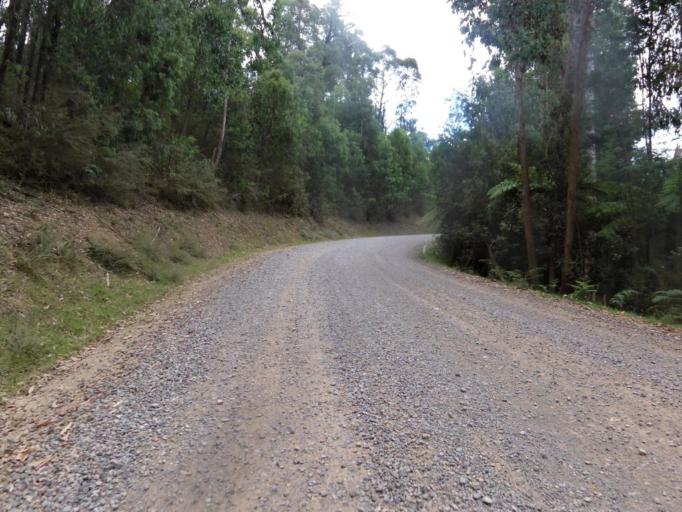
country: AU
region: Victoria
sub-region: Yarra Ranges
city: Healesville
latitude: -37.4111
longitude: 145.5609
